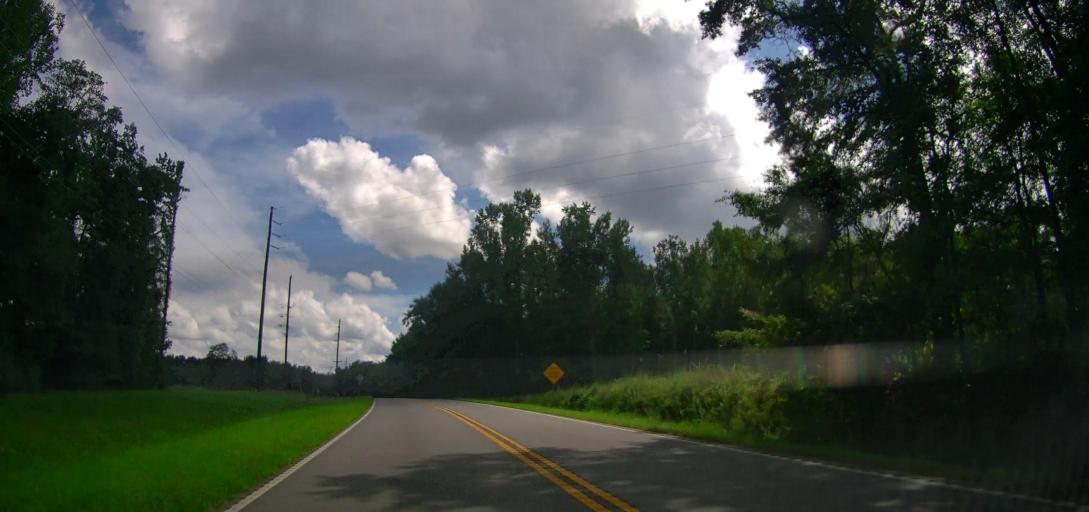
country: US
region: Georgia
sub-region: Talbot County
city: Talbotton
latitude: 32.6211
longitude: -84.4885
